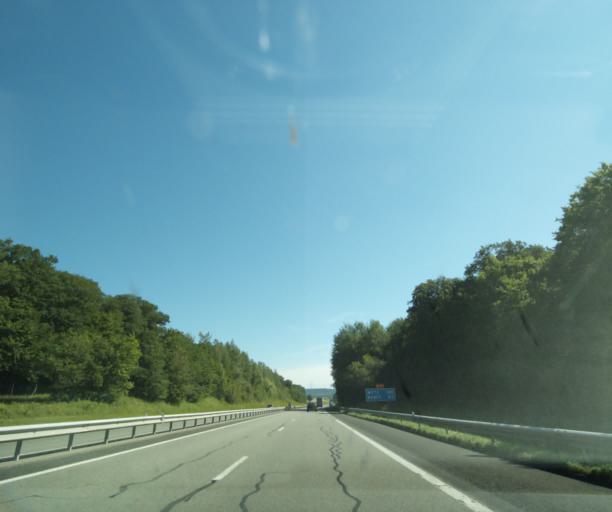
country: FR
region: Lorraine
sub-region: Departement des Vosges
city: Lamarche
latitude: 48.1535
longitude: 5.6935
